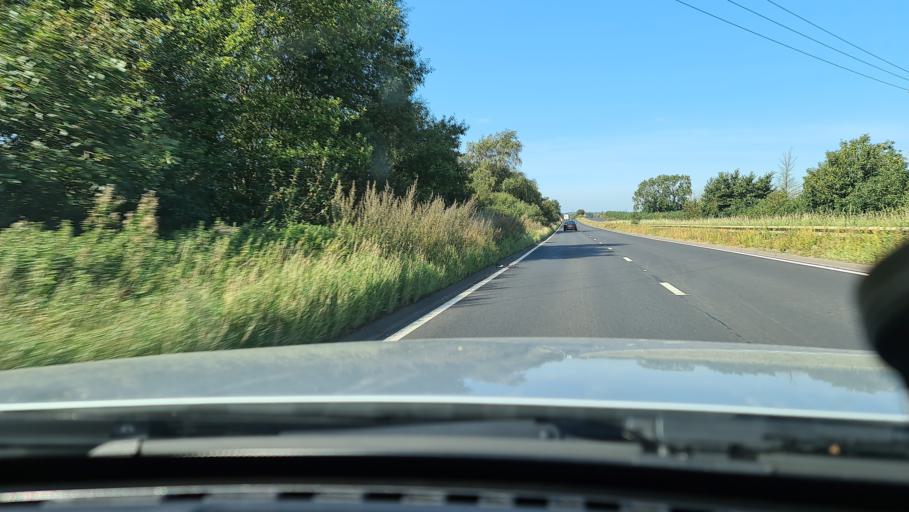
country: GB
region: England
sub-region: Leicestershire
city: Sapcote
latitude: 52.4969
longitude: -1.3123
